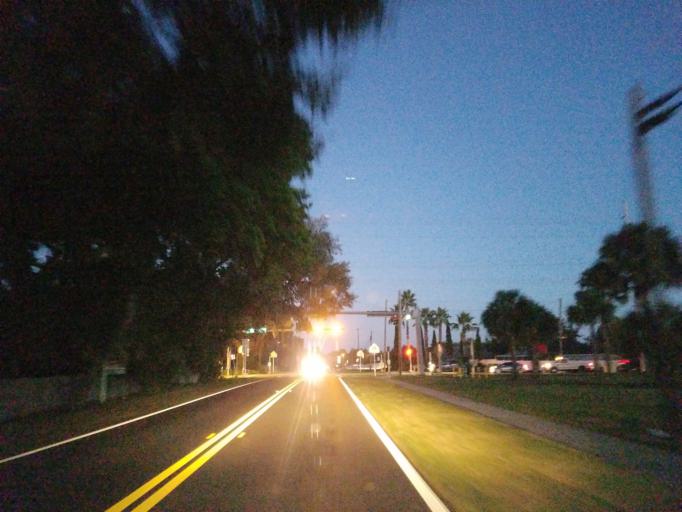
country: US
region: Florida
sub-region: Hillsborough County
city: Bloomingdale
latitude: 27.9083
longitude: -82.2284
